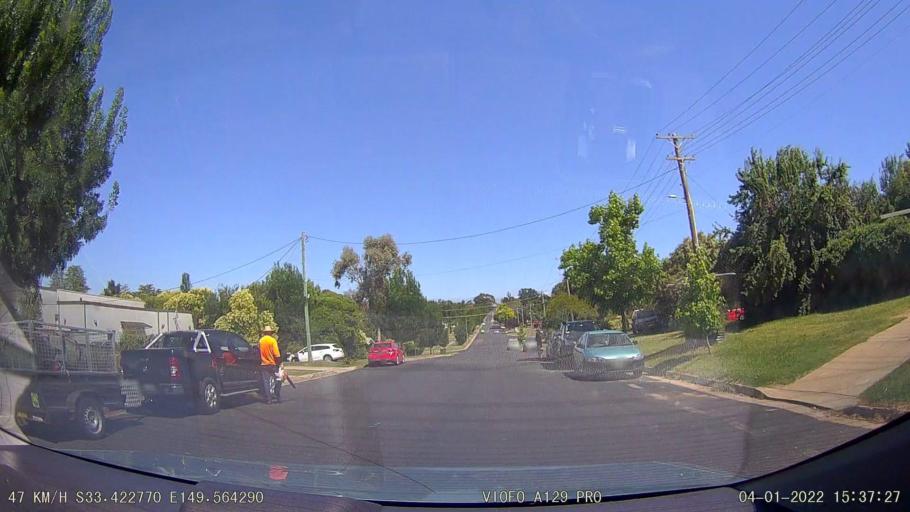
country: AU
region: New South Wales
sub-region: Bathurst Regional
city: Bathurst
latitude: -33.4226
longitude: 149.5641
